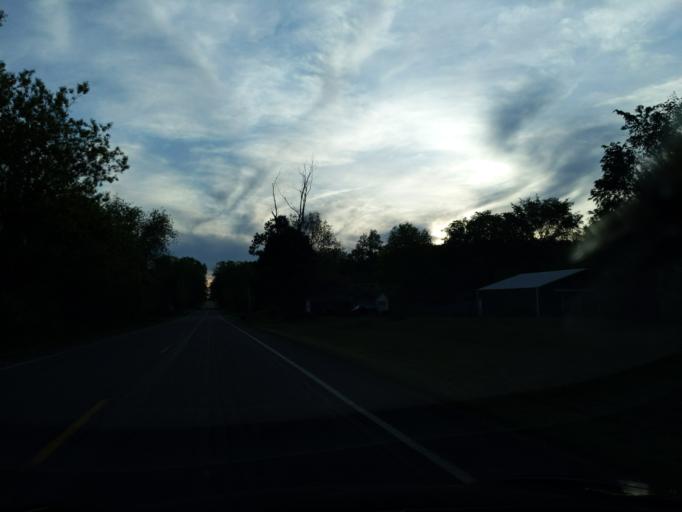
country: US
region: Michigan
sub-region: Ingham County
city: Williamston
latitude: 42.6009
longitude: -84.3290
